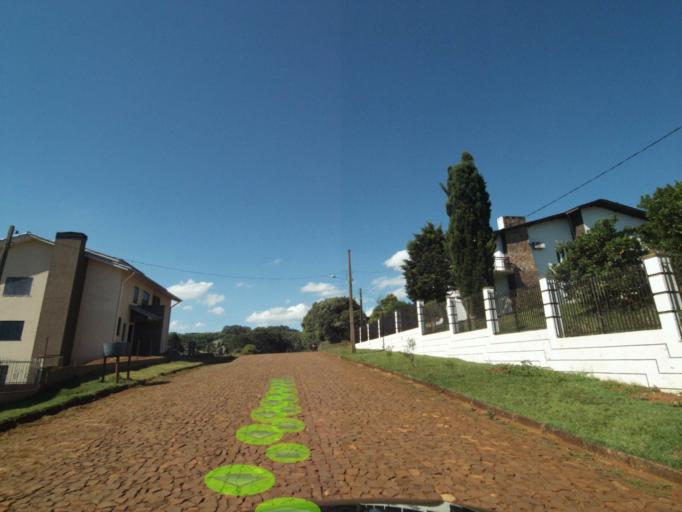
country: BR
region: Parana
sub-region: Coronel Vivida
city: Coronel Vivida
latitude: -26.1453
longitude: -52.3795
